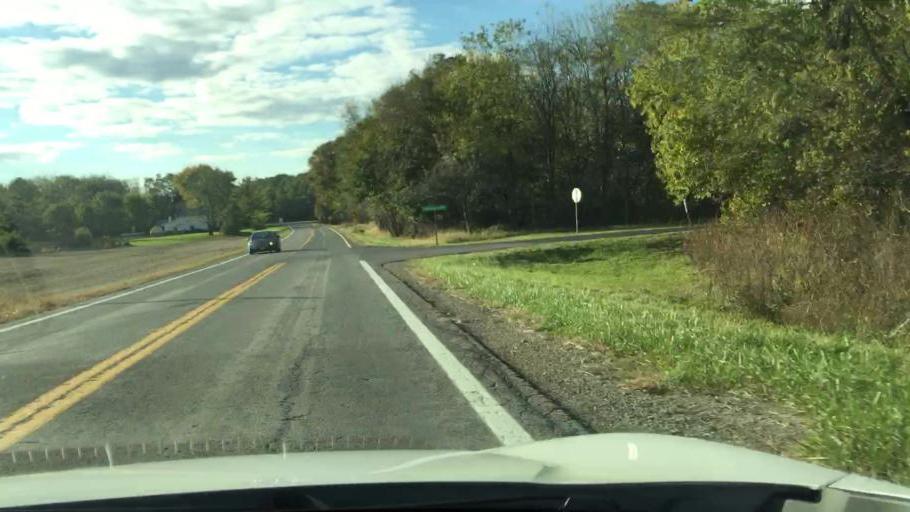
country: US
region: Ohio
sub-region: Champaign County
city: North Lewisburg
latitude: 40.2280
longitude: -83.5226
